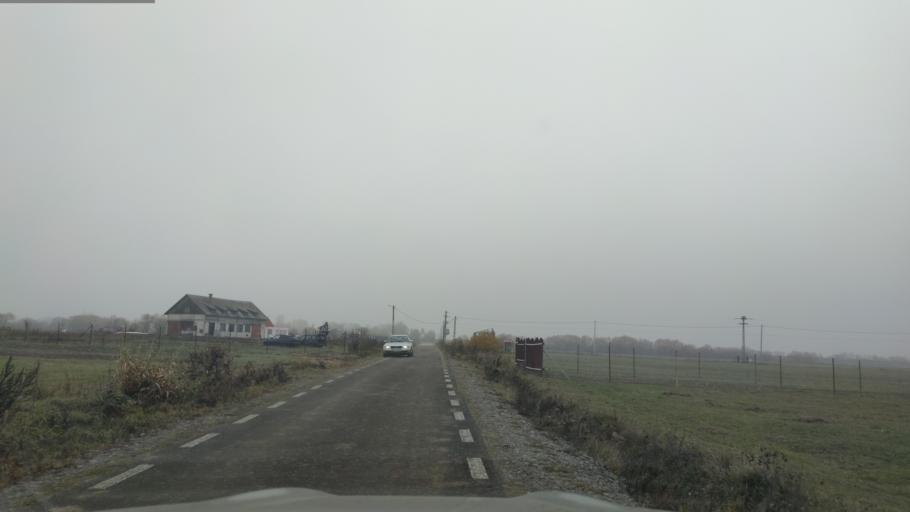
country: RO
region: Harghita
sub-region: Comuna Remetea
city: Remetea
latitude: 46.8089
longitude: 25.4230
